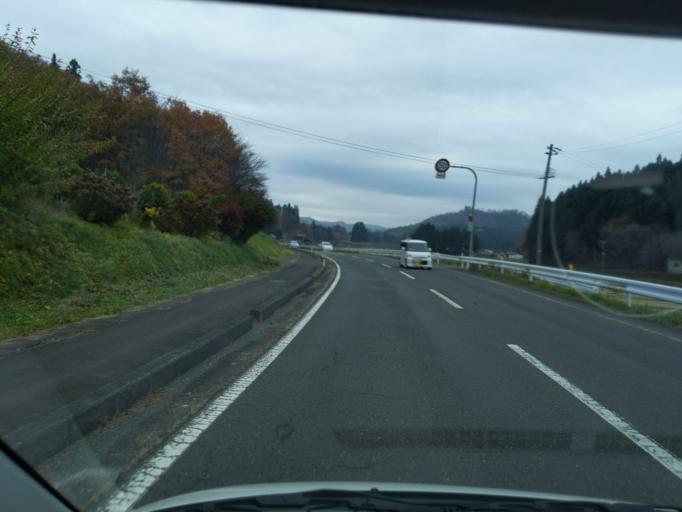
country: JP
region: Iwate
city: Kitakami
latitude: 39.2958
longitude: 141.1824
